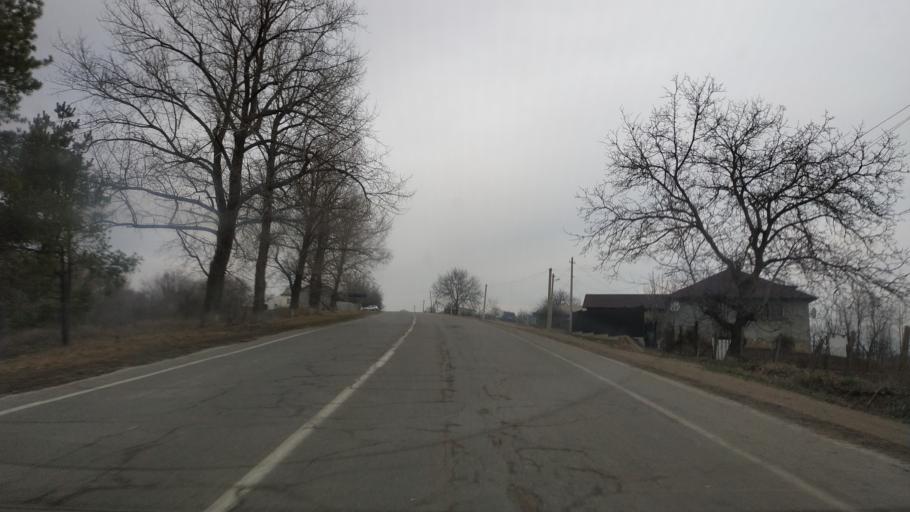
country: MD
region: Hincesti
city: Hincesti
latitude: 46.7199
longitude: 28.5121
